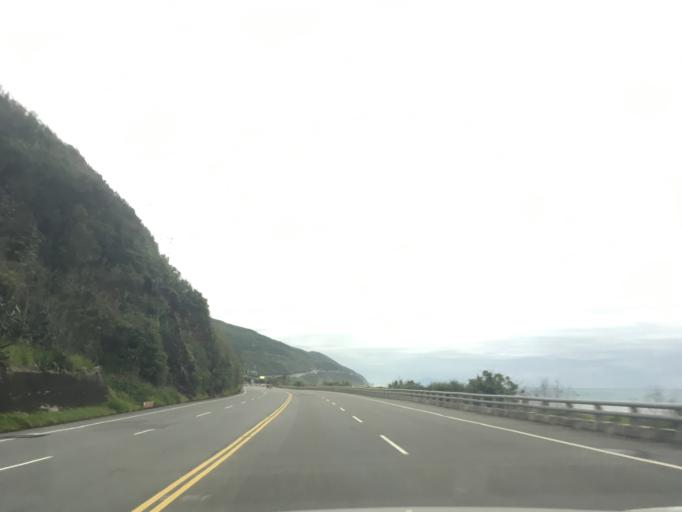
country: TW
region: Taiwan
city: Hengchun
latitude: 22.3694
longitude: 120.9099
